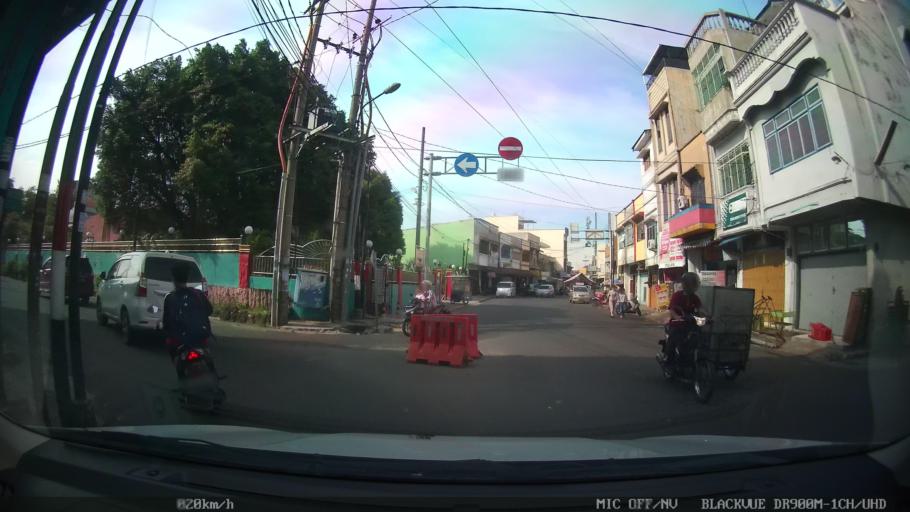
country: ID
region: North Sumatra
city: Binjai
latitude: 3.6032
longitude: 98.4869
